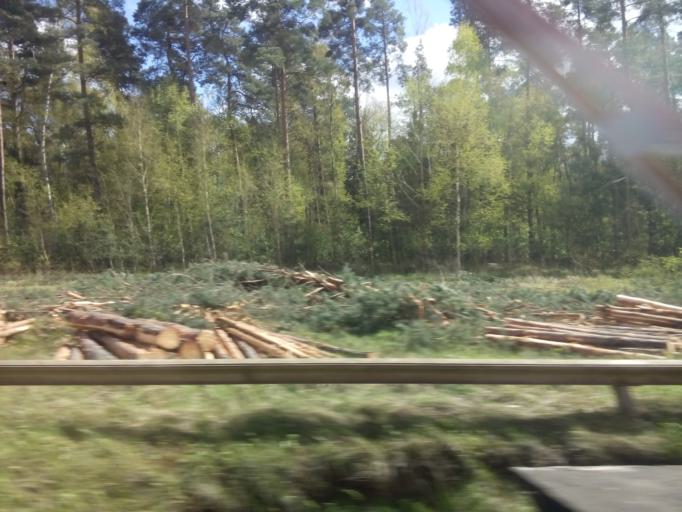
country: DE
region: Brandenburg
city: Falkensee
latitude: 52.6223
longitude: 13.1054
